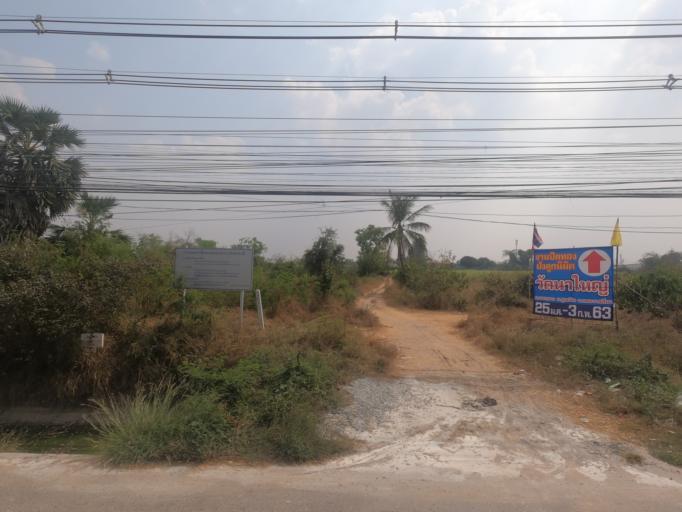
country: TH
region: Nakhon Ratchasima
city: Kham Thale So
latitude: 14.9012
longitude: 101.9059
